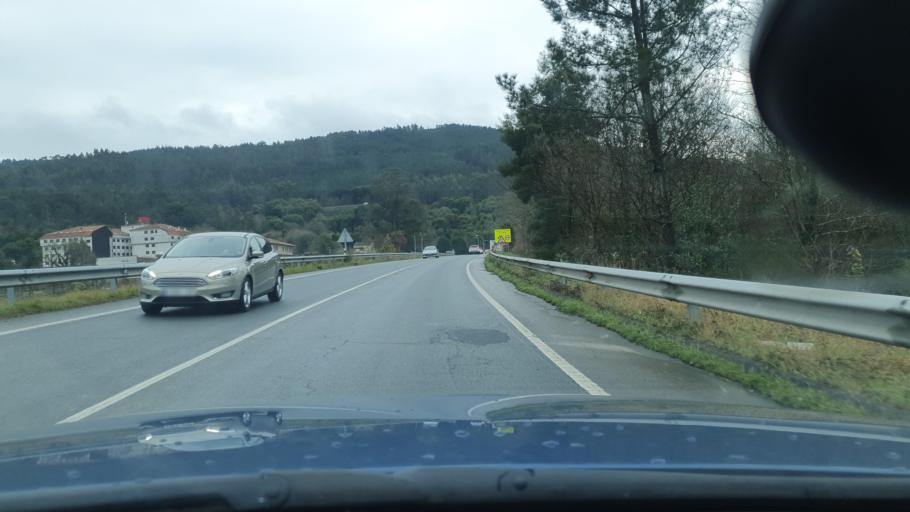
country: ES
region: Galicia
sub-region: Provincia da Coruna
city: Padron
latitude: 42.7566
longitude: -8.6561
